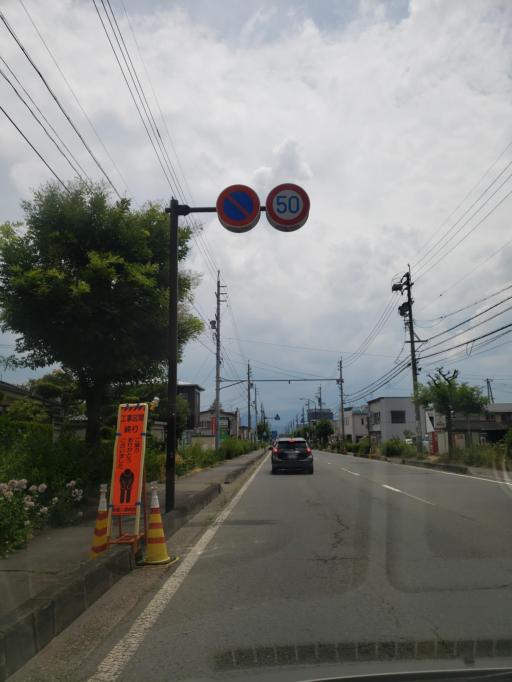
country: JP
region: Nagano
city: Nagano-shi
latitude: 36.6587
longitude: 138.2299
